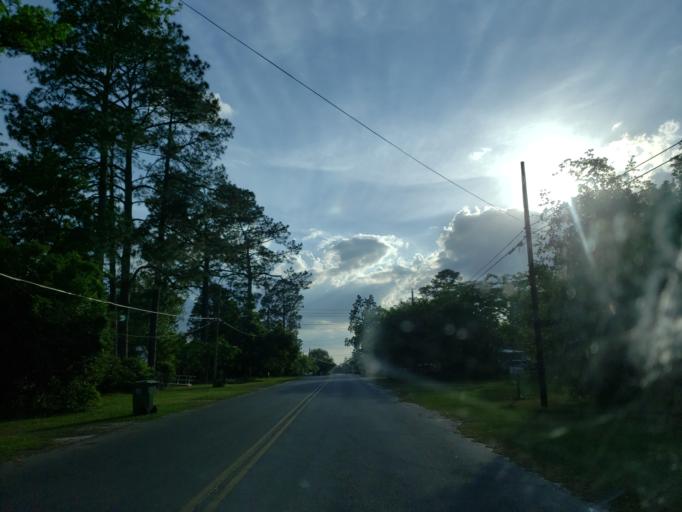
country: US
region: Georgia
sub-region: Cook County
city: Adel
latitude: 31.1394
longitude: -83.4196
